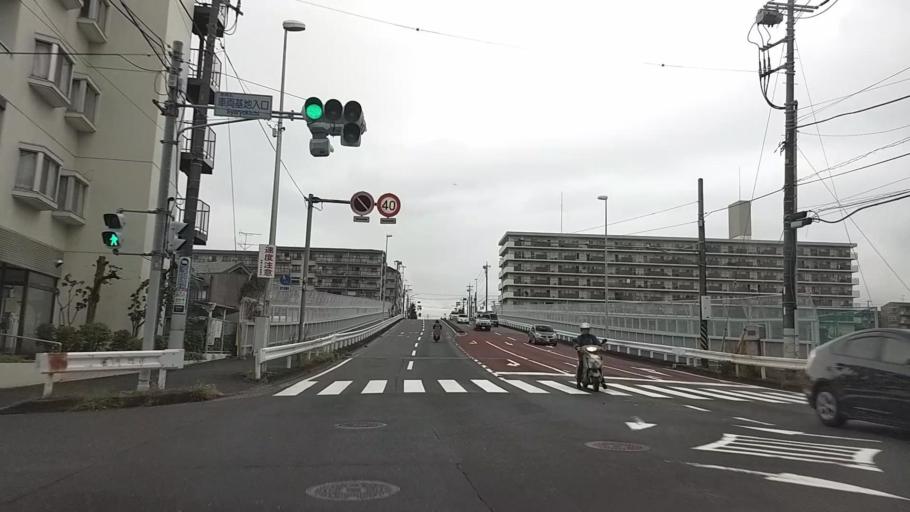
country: JP
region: Kanagawa
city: Kamakura
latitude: 35.3937
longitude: 139.5676
